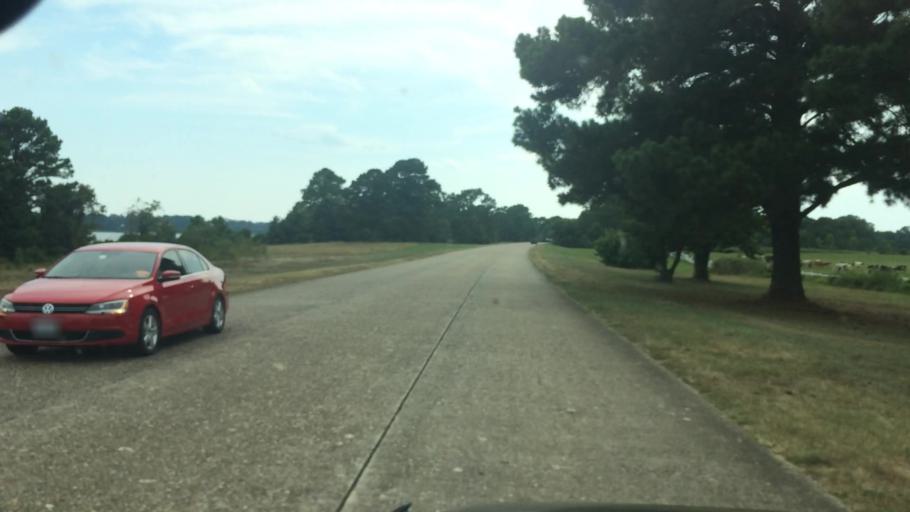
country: US
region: Virginia
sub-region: City of Williamsburg
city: Williamsburg
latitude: 37.2141
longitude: -76.7251
